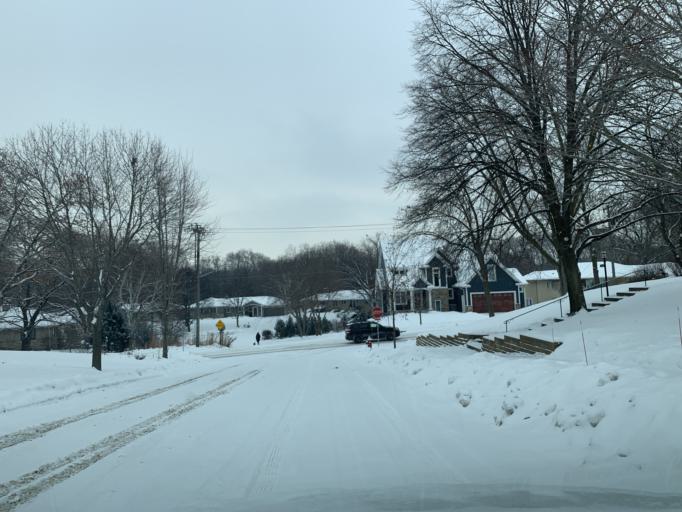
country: US
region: Minnesota
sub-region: Hennepin County
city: Saint Louis Park
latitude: 44.9328
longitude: -93.3303
